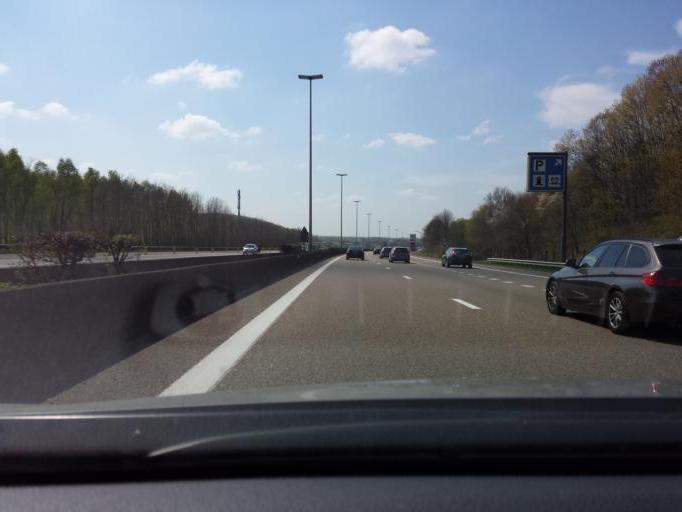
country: BE
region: Flanders
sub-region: Provincie Vlaams-Brabant
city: Holsbeek
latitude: 50.9529
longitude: 4.7981
